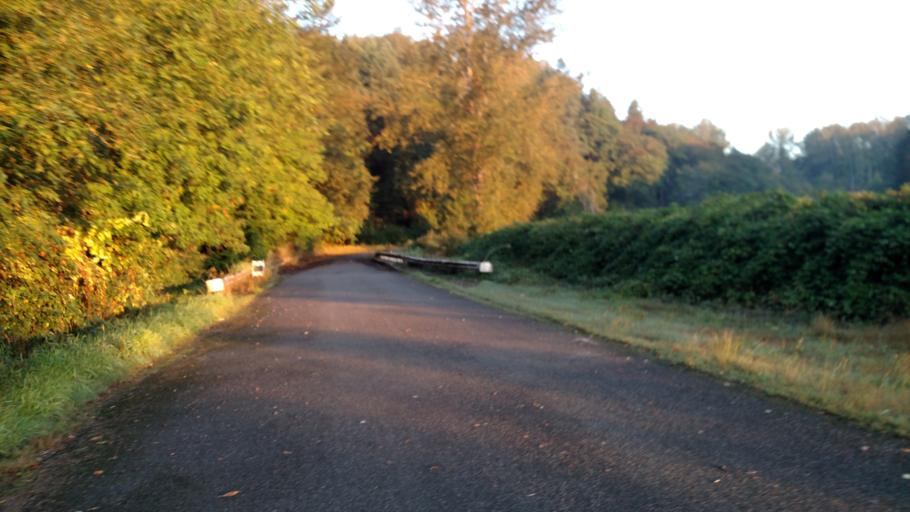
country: US
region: Washington
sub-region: King County
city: Kent
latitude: 47.3919
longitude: -122.2733
